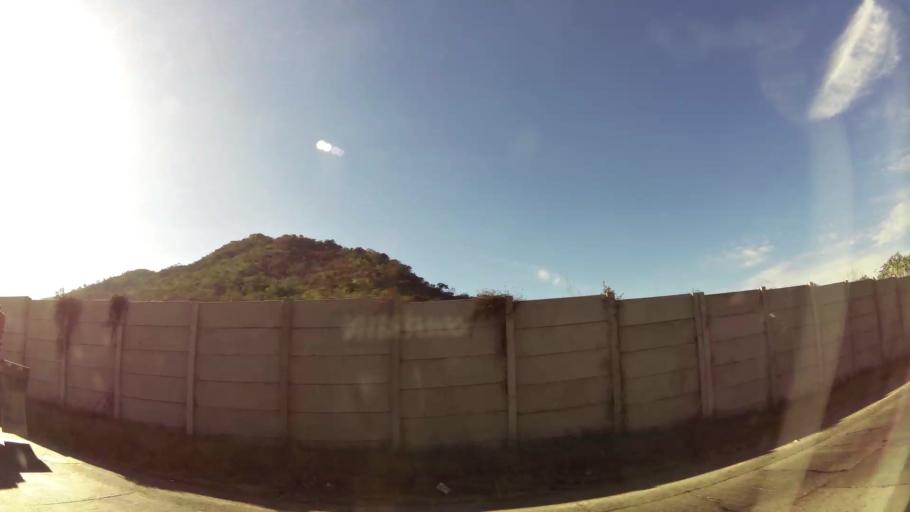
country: SV
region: Santa Ana
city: Santa Ana
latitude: 14.0537
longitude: -89.5157
